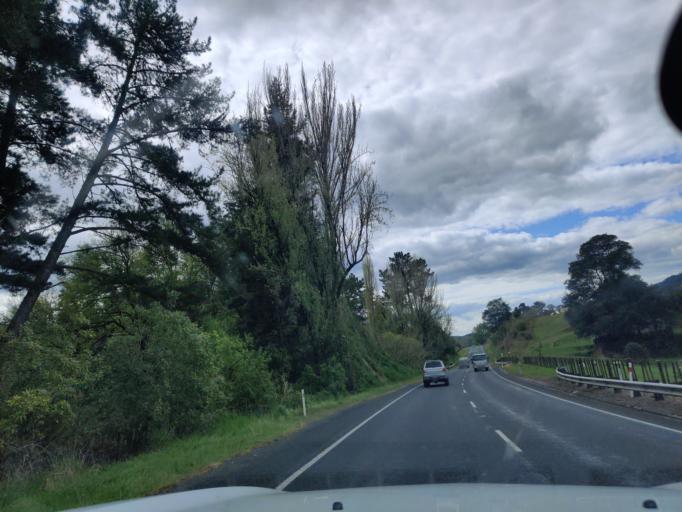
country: NZ
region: Waikato
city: Turangi
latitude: -38.8627
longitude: 175.2361
